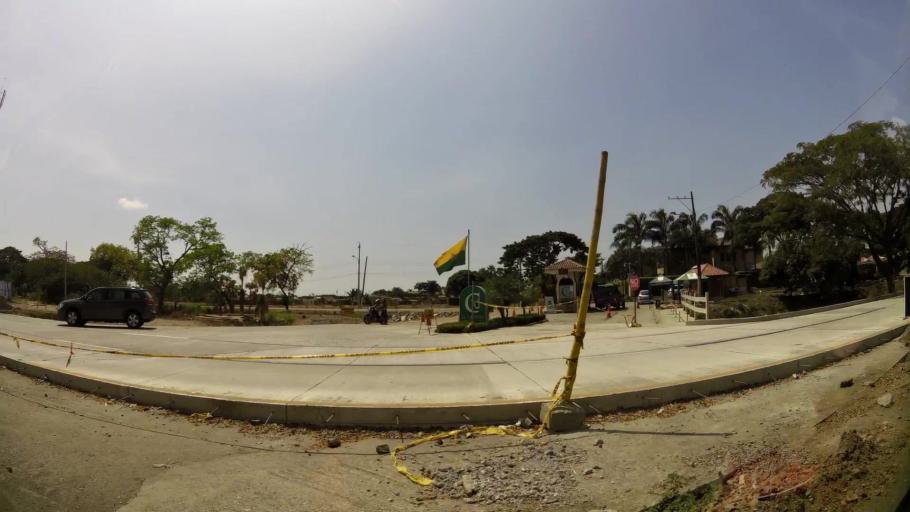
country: EC
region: Guayas
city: Eloy Alfaro
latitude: -2.0749
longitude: -79.8622
